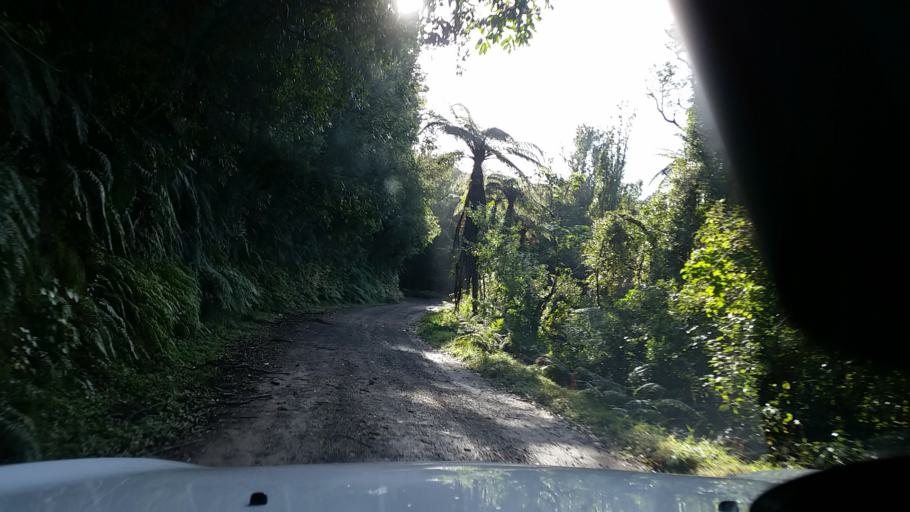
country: NZ
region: Bay of Plenty
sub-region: Kawerau District
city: Kawerau
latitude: -38.0192
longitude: 176.5884
